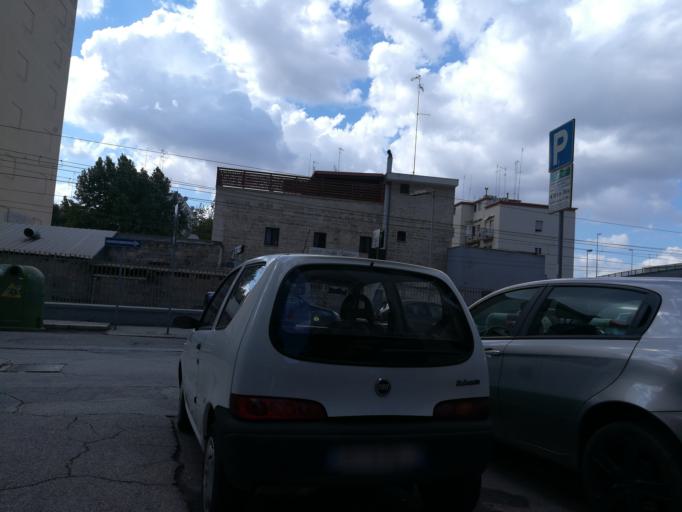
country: IT
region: Apulia
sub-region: Provincia di Bari
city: Bari
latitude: 41.1170
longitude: 16.8895
